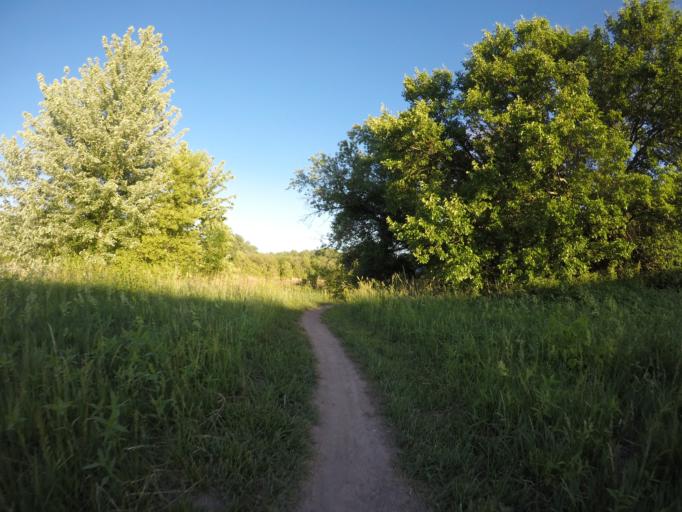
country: US
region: Kansas
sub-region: Riley County
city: Manhattan
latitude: 39.1781
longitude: -96.5544
